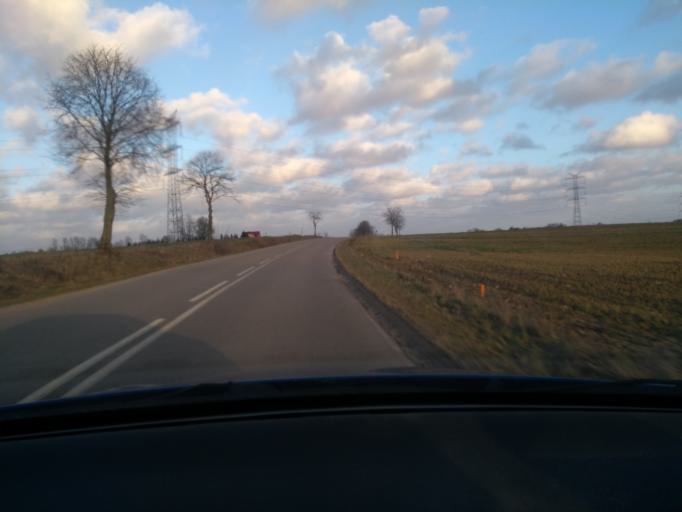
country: PL
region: Pomeranian Voivodeship
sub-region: Powiat kartuski
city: Przodkowo
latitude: 54.4171
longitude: 18.2930
